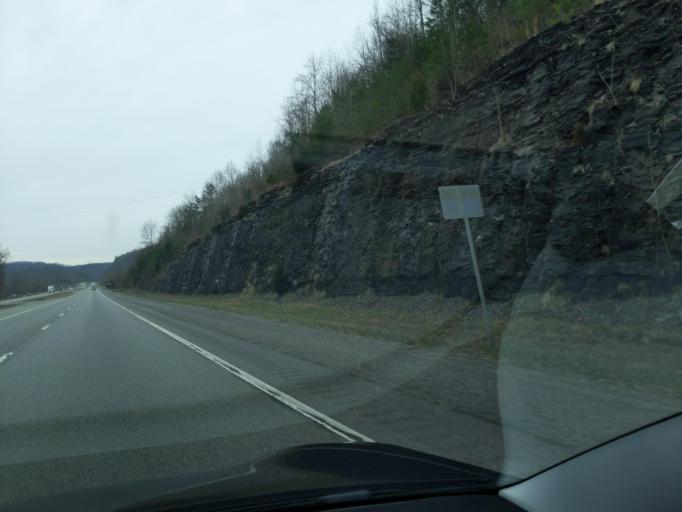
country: US
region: Kentucky
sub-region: Bell County
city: Pineville
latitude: 36.8177
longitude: -83.7703
